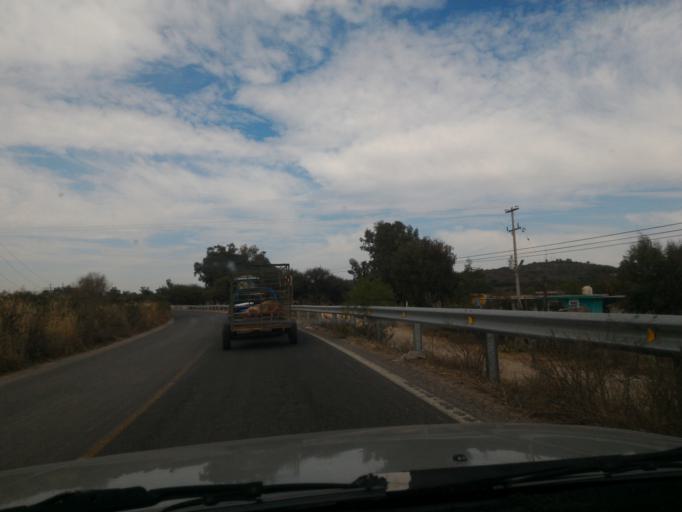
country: MX
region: Guanajuato
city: Ciudad Manuel Doblado
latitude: 20.7964
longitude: -101.9848
